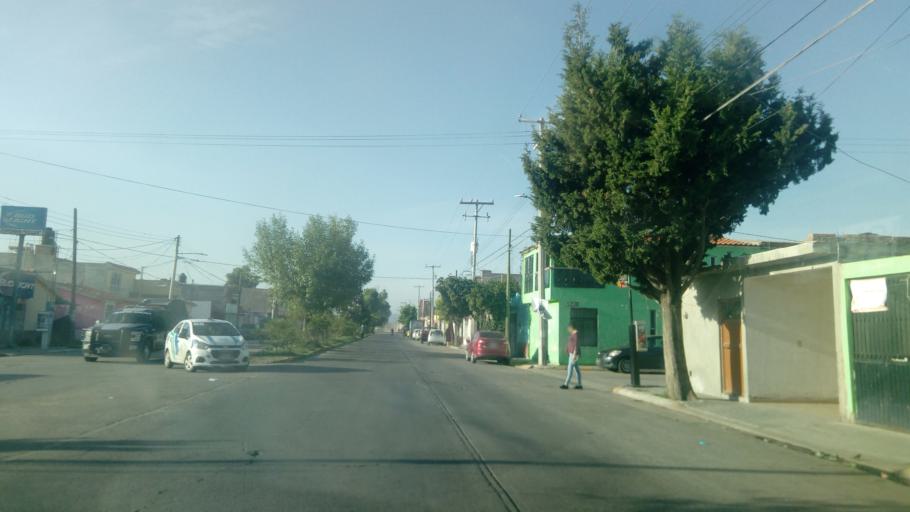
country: MX
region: Durango
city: Victoria de Durango
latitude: 24.0595
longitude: -104.5847
